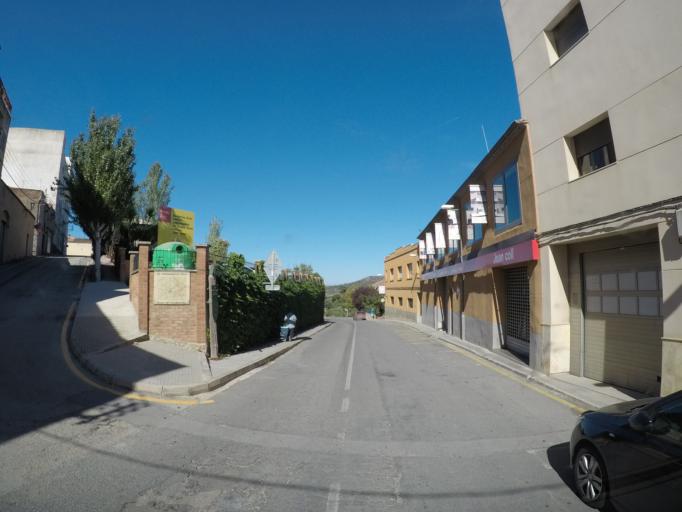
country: ES
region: Catalonia
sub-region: Provincia de Tarragona
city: Falset
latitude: 41.1467
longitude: 0.8205
